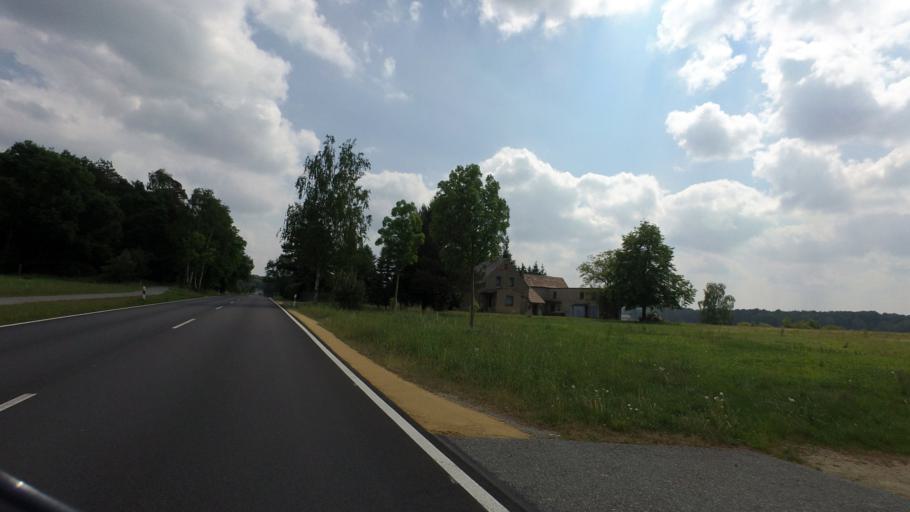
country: DE
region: Saxony
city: Rietschen
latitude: 51.3656
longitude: 14.7984
